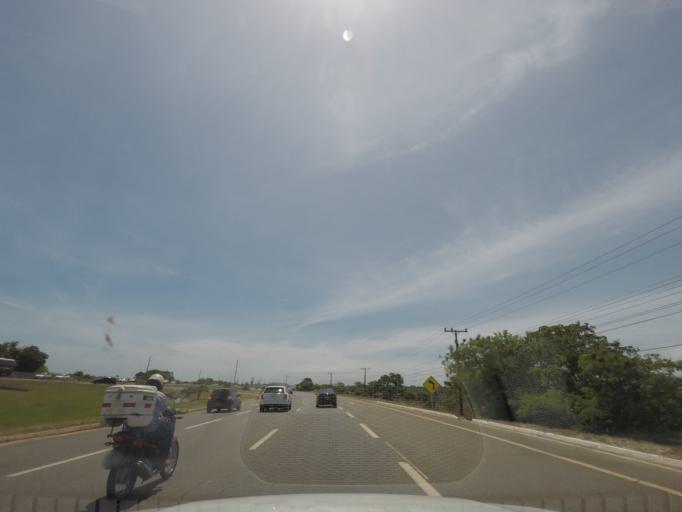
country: BR
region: Bahia
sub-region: Camacari
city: Camacari
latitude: -12.7160
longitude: -38.1514
